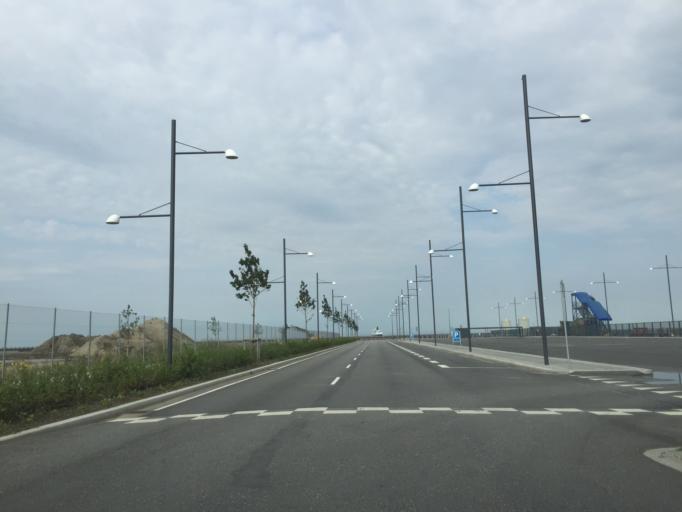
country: DK
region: Capital Region
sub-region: Gentofte Kommune
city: Charlottenlund
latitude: 55.7177
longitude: 12.6281
